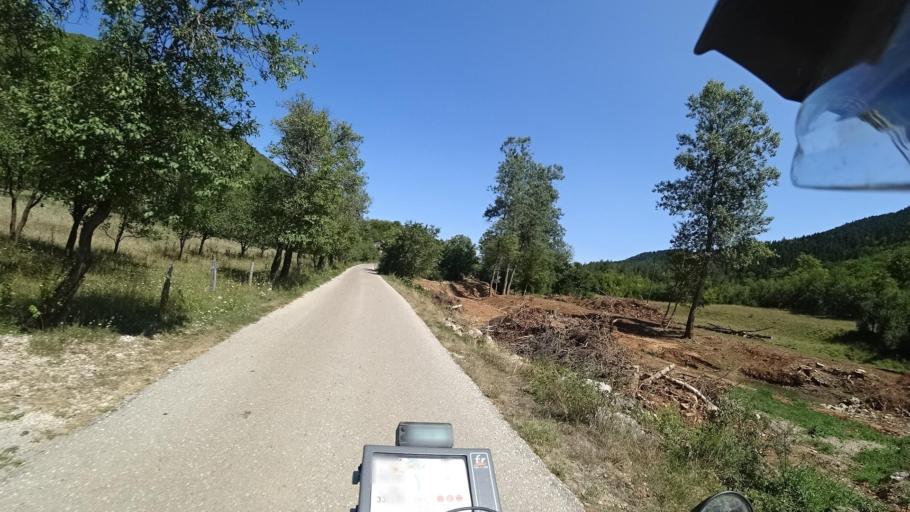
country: HR
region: Licko-Senjska
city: Popovaca
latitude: 44.7046
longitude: 15.2371
